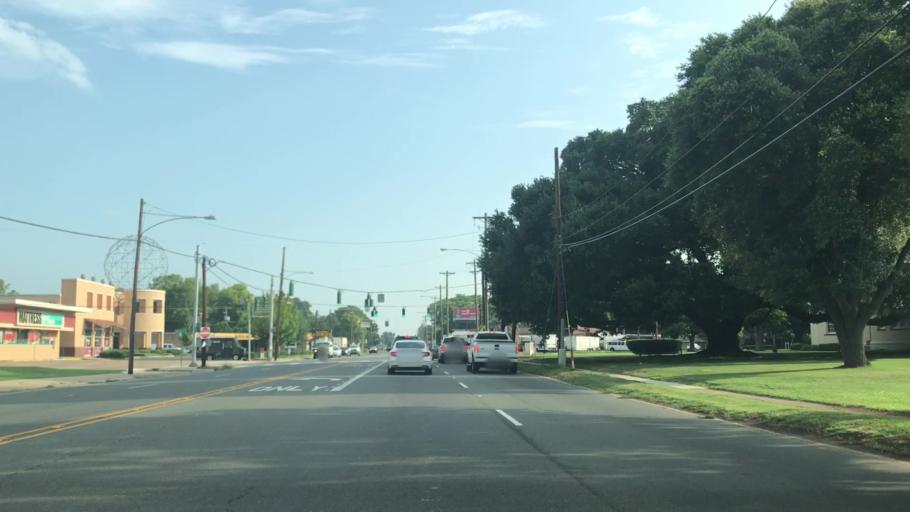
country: US
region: Louisiana
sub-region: Bossier Parish
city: Bossier City
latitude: 32.4663
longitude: -93.7221
